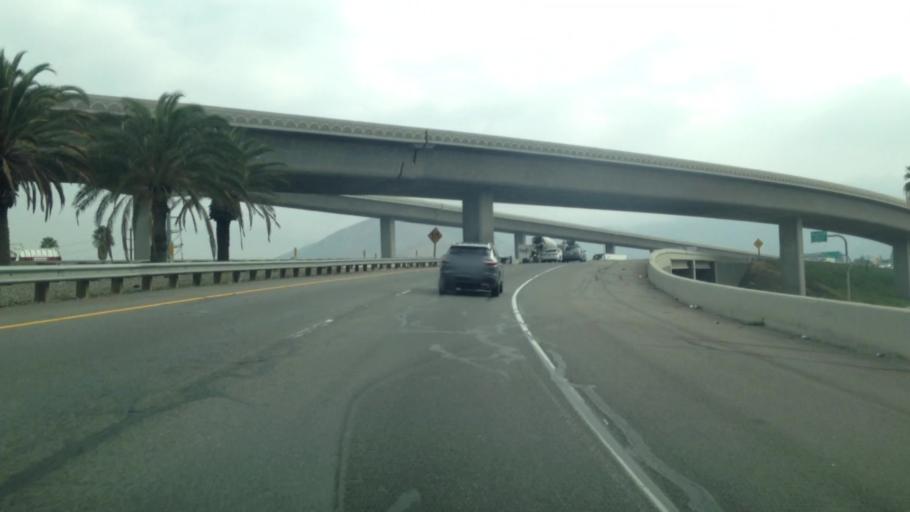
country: US
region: California
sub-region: Riverside County
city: Highgrove
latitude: 33.9921
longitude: -117.3561
